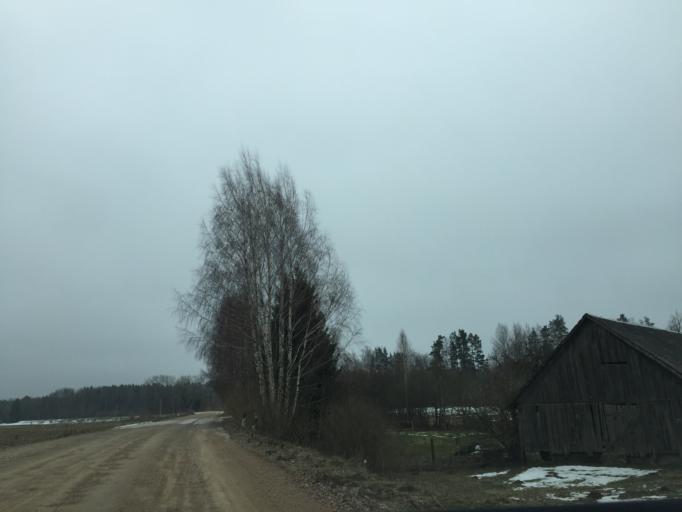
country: LV
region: Ozolnieku
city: Ozolnieki
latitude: 56.6350
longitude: 23.8008
